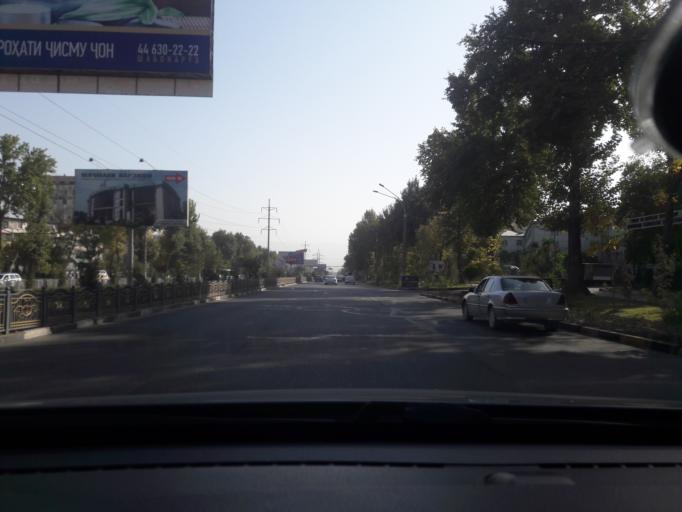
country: TJ
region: Dushanbe
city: Dushanbe
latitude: 38.5289
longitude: 68.7618
